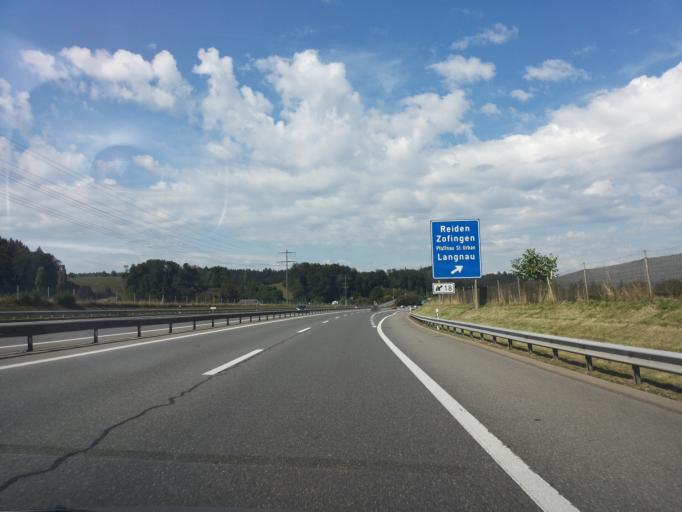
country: CH
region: Lucerne
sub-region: Willisau District
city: Reiden
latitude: 47.2405
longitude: 7.9587
